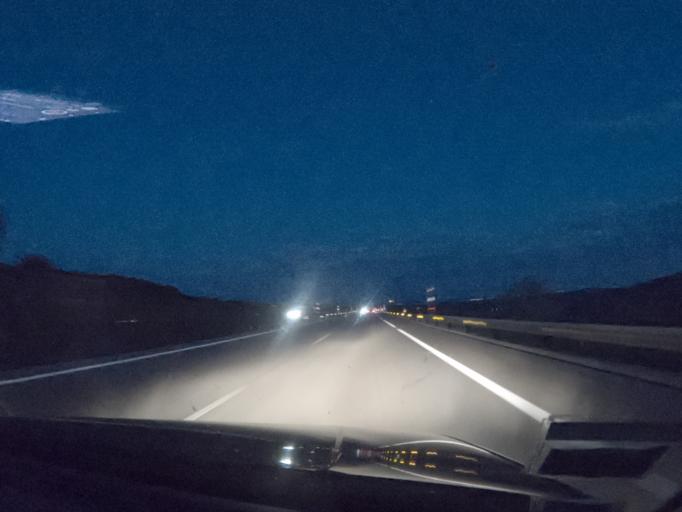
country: ES
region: Castille and Leon
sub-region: Provincia de Leon
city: Brazuelo
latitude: 42.5636
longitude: -6.2055
